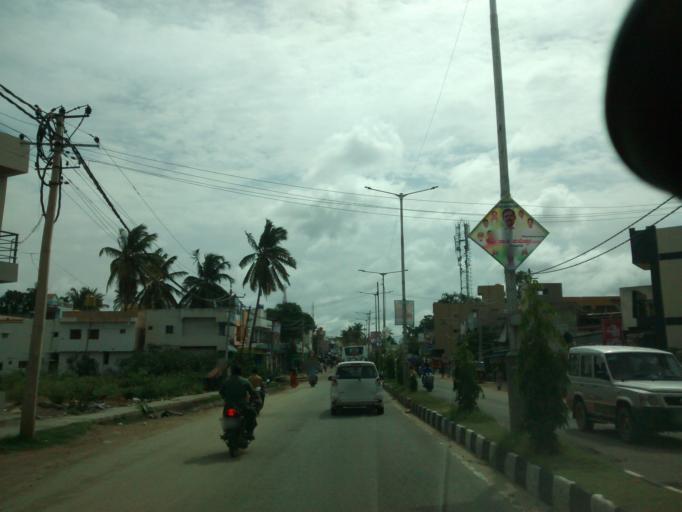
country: IN
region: Karnataka
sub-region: Tumkur
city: Koratagere
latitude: 13.5186
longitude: 77.2339
